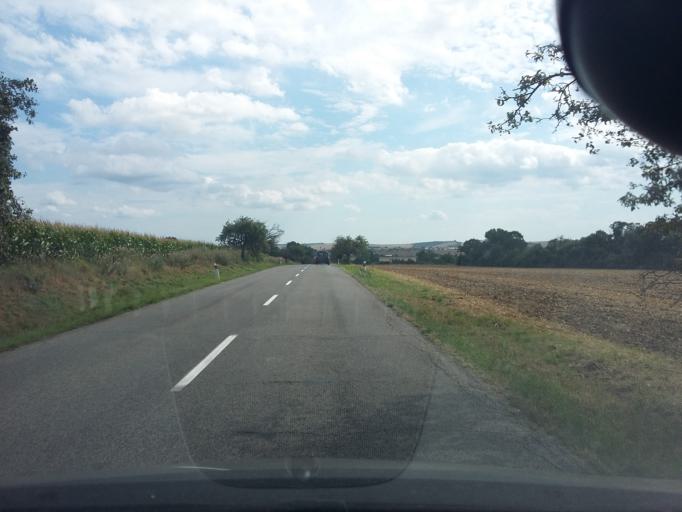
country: SK
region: Trnavsky
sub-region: Okres Skalica
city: Holic
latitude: 48.7492
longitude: 17.1706
